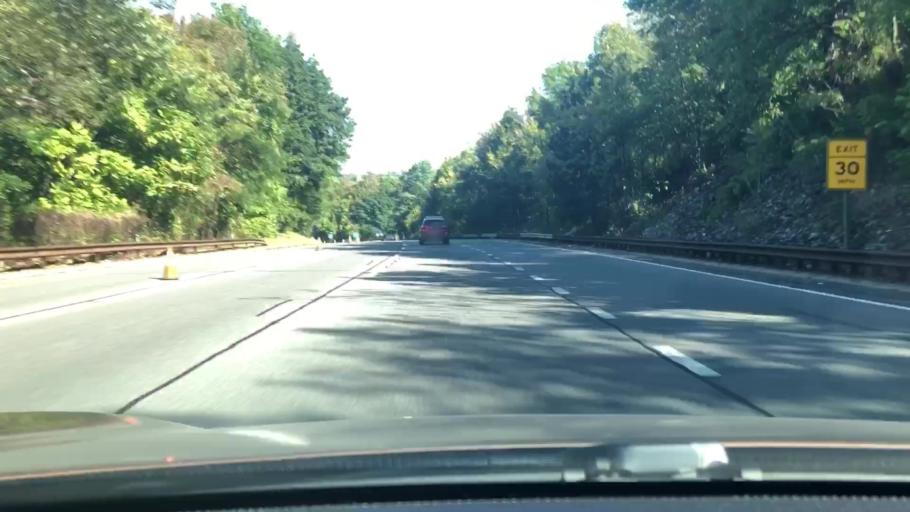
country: US
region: New York
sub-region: Westchester County
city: Greenville
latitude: 40.9837
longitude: -73.8388
